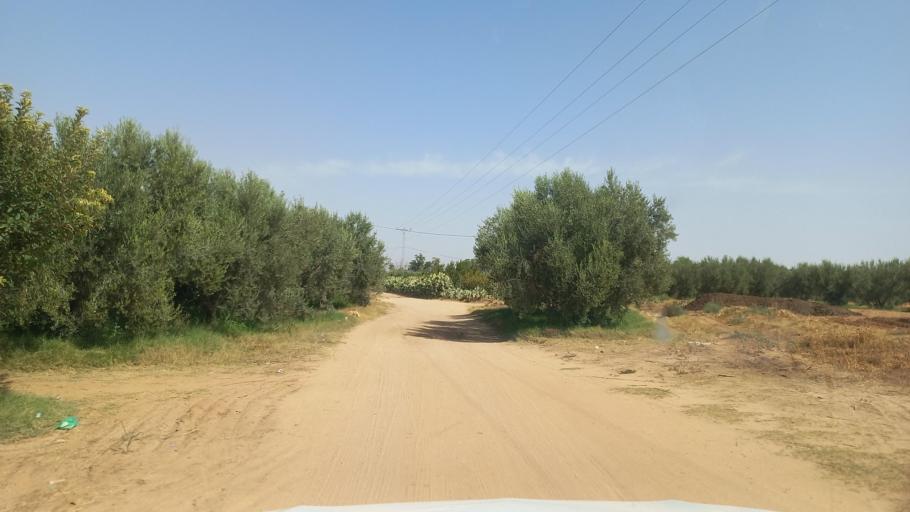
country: TN
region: Al Qasrayn
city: Kasserine
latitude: 35.2579
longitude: 9.0435
